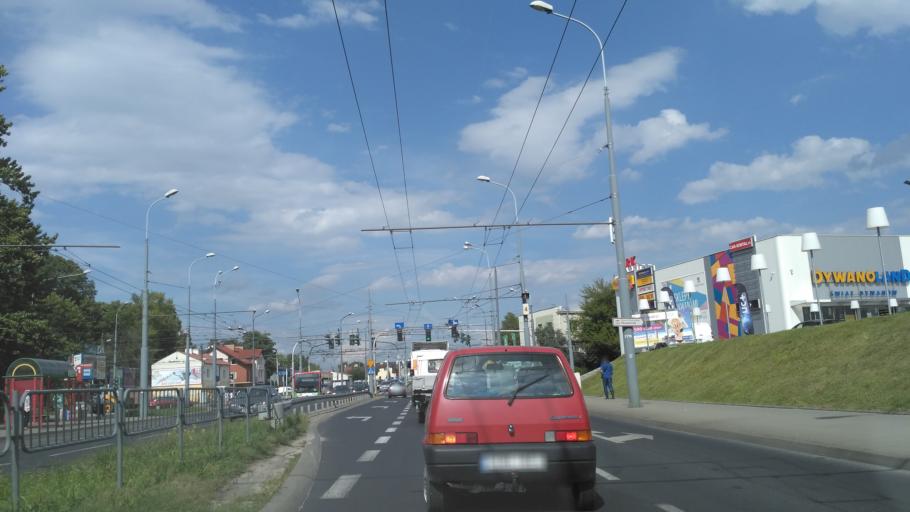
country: PL
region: Lublin Voivodeship
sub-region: Powiat lubelski
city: Lublin
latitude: 51.2358
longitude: 22.5757
